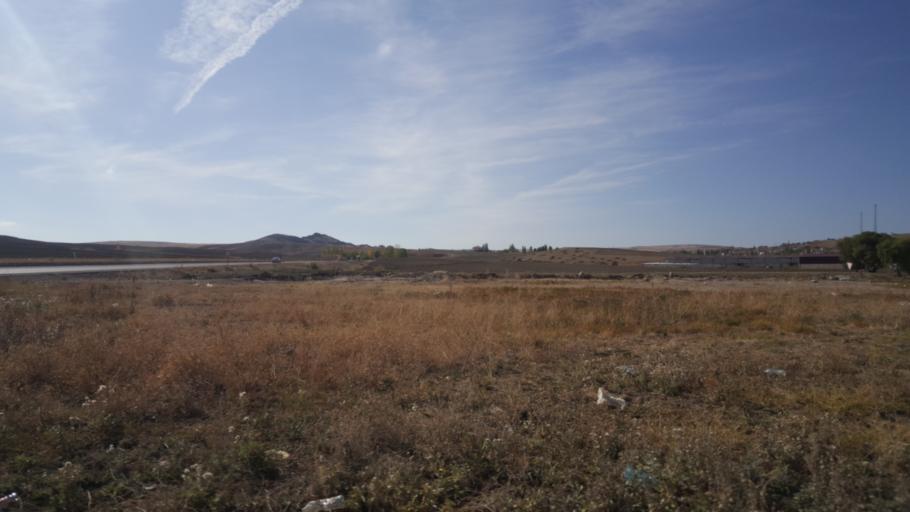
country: TR
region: Ankara
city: Yenice
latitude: 39.3736
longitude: 32.7258
